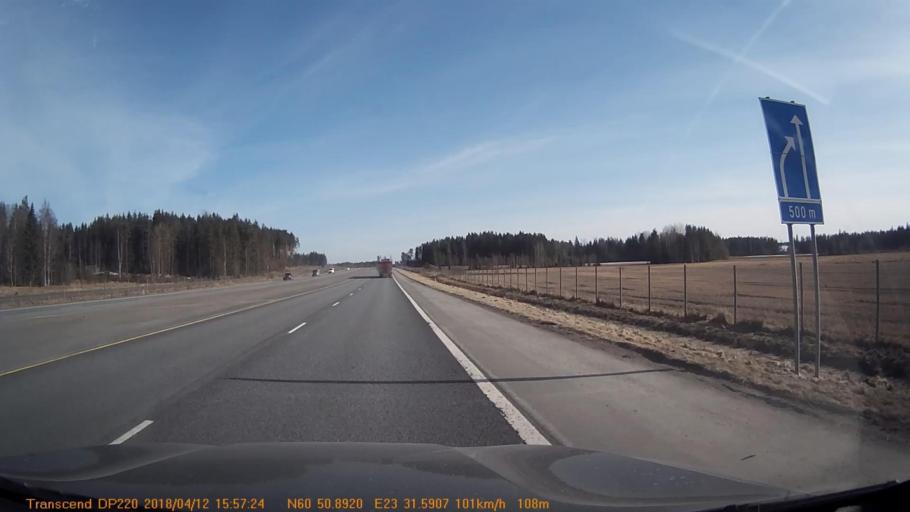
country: FI
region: Haeme
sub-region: Forssa
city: Jokioinen
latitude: 60.8480
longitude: 23.5268
